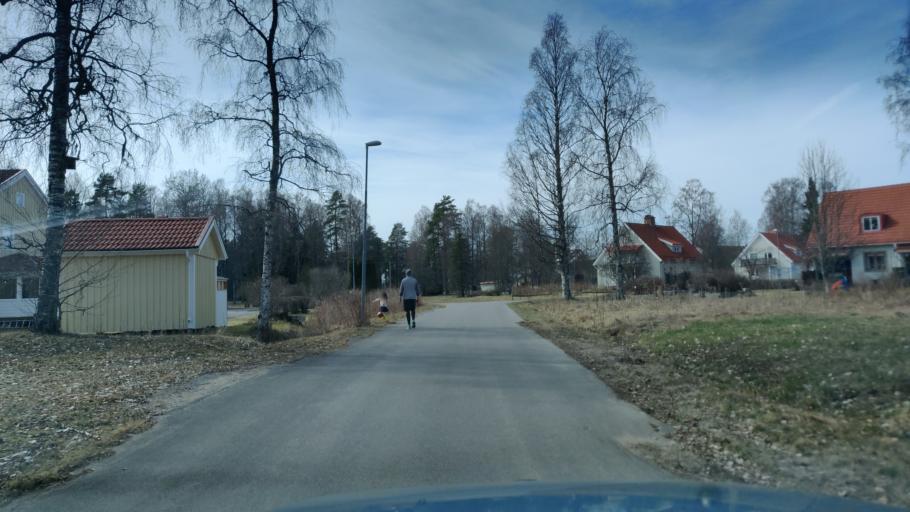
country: SE
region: Vaermland
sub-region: Hagfors Kommun
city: Hagfors
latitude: 60.0230
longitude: 13.6235
